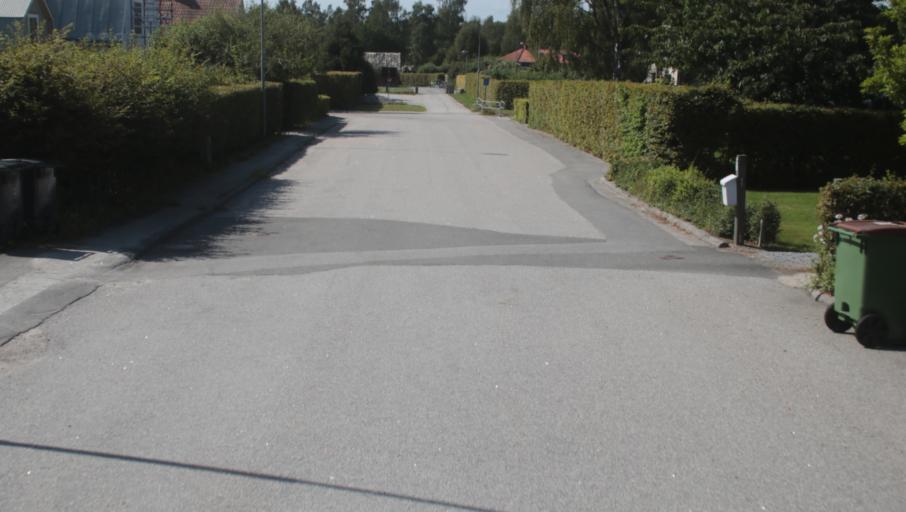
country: SE
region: Blekinge
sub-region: Karlshamns Kommun
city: Karlshamn
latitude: 56.2097
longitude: 14.8334
